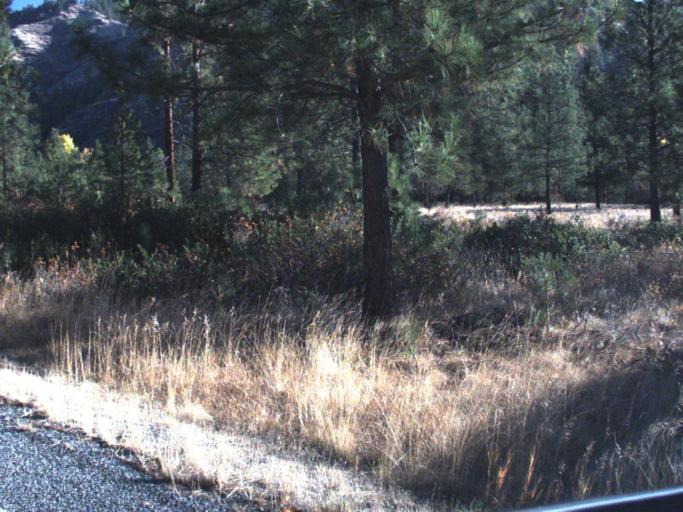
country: US
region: Washington
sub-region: Okanogan County
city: Coulee Dam
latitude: 48.1186
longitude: -118.6962
